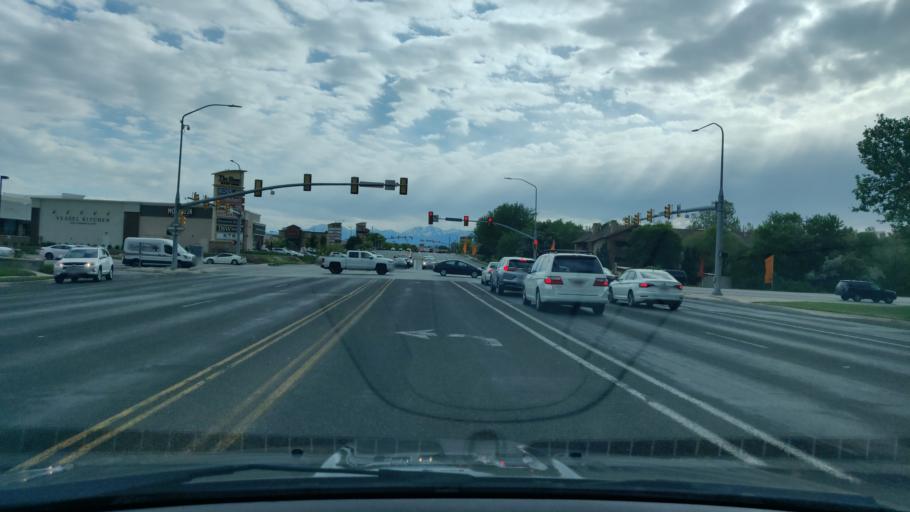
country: US
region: Utah
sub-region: Salt Lake County
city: Little Cottonwood Creek Valley
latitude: 40.6251
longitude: -111.8595
